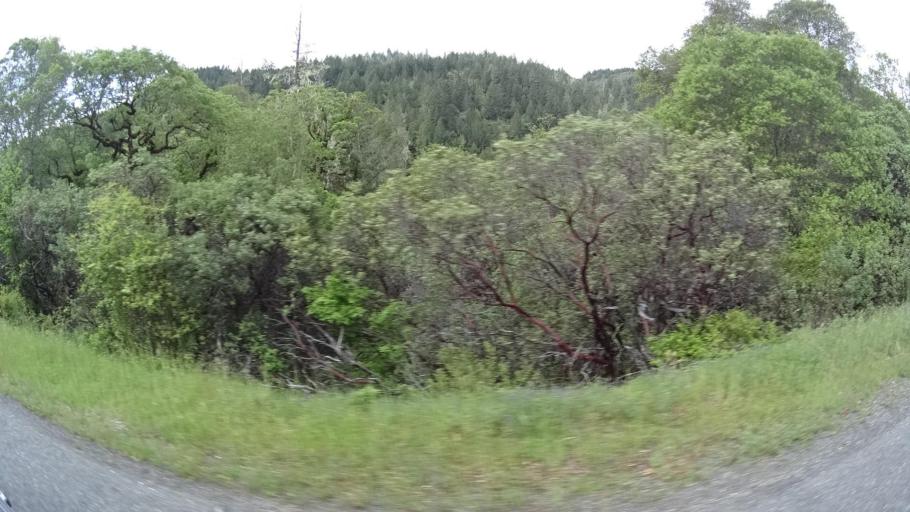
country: US
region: California
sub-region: Humboldt County
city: Redway
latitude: 40.2000
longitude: -123.5935
